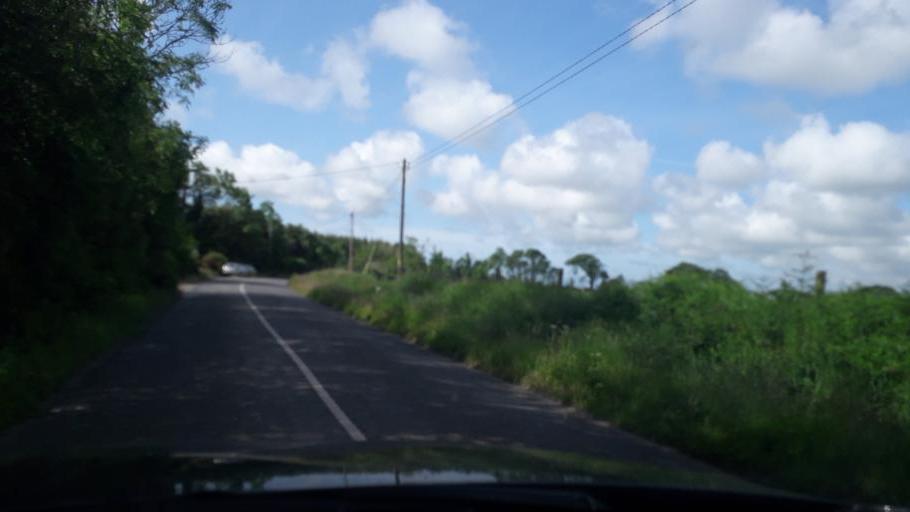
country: IE
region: Leinster
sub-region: Loch Garman
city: Loch Garman
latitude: 52.2801
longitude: -6.5403
